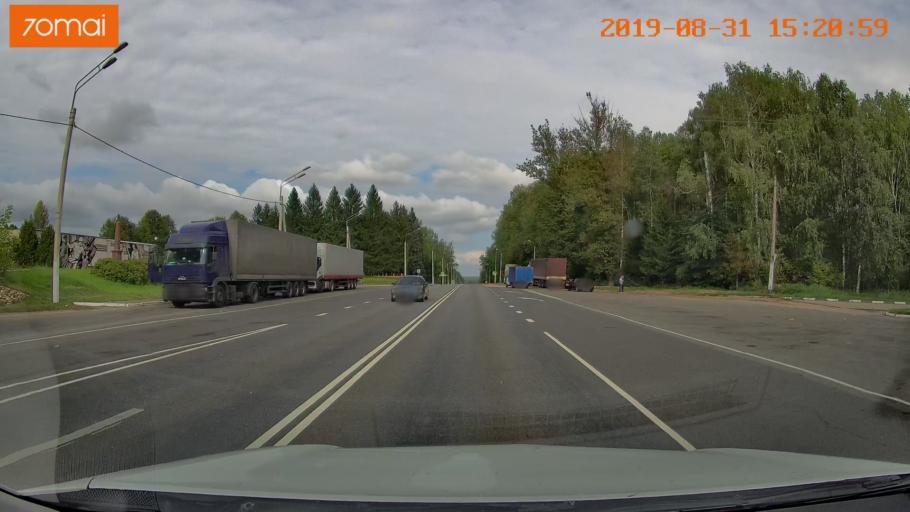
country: RU
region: Kaluga
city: Baryatino
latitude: 54.4938
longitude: 34.4458
